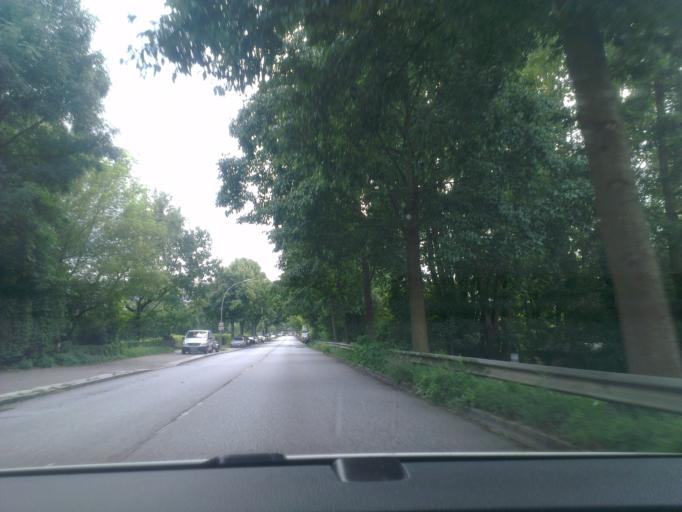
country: DE
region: Hamburg
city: Steilshoop
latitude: 53.5963
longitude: 10.0725
